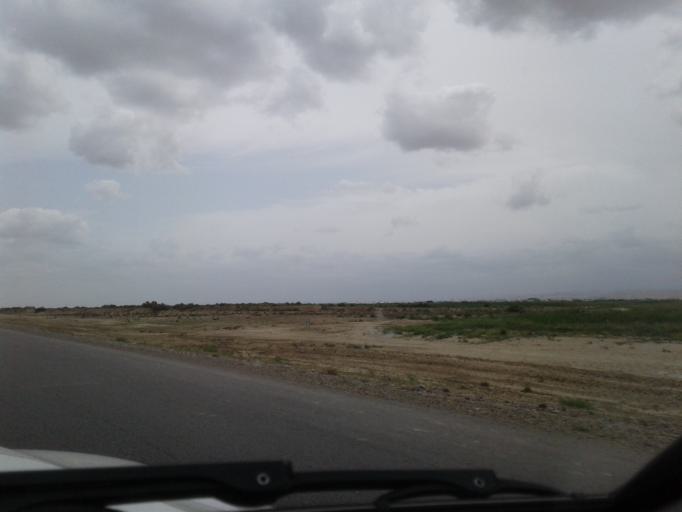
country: IR
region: Razavi Khorasan
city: Dargaz
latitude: 37.5768
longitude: 59.3203
